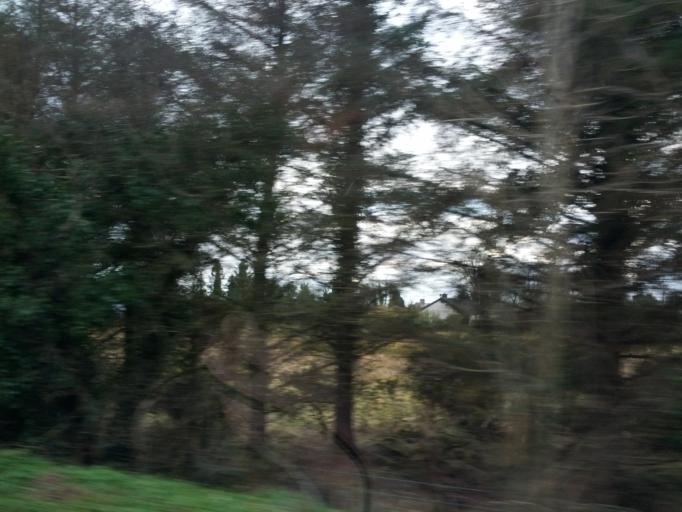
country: IE
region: Connaught
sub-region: County Galway
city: Athenry
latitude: 53.3974
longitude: -8.6233
